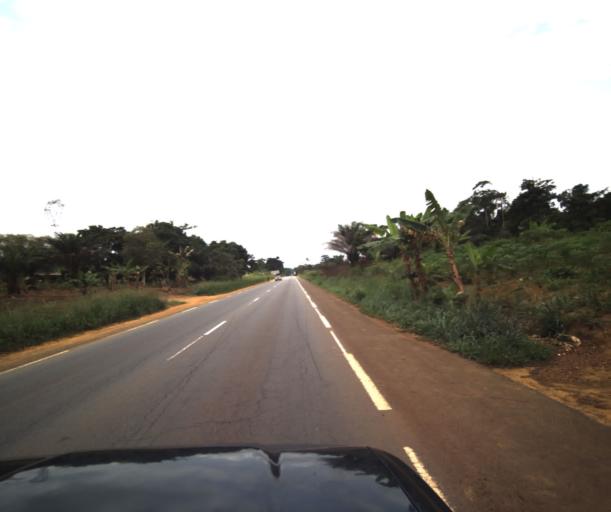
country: CM
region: Centre
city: Eseka
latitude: 3.8709
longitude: 10.9105
